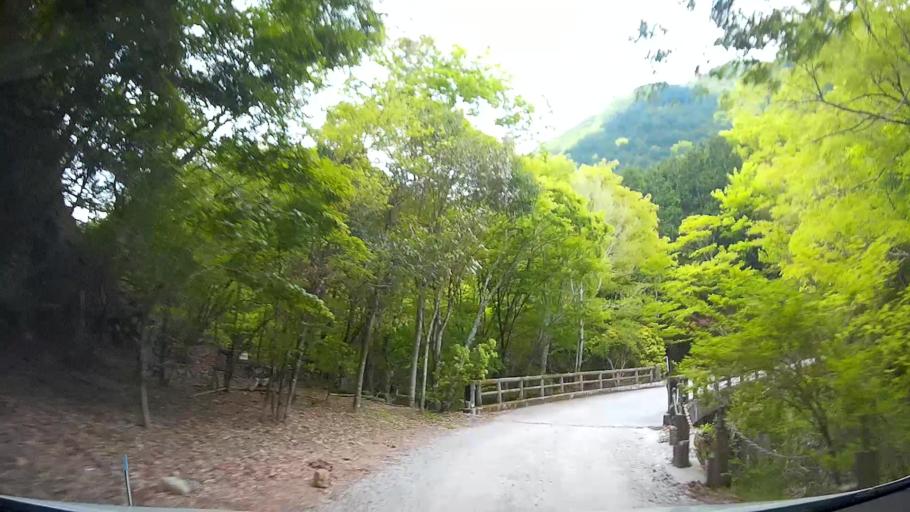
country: JP
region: Shizuoka
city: Shimoda
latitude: 34.8365
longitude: 138.9355
